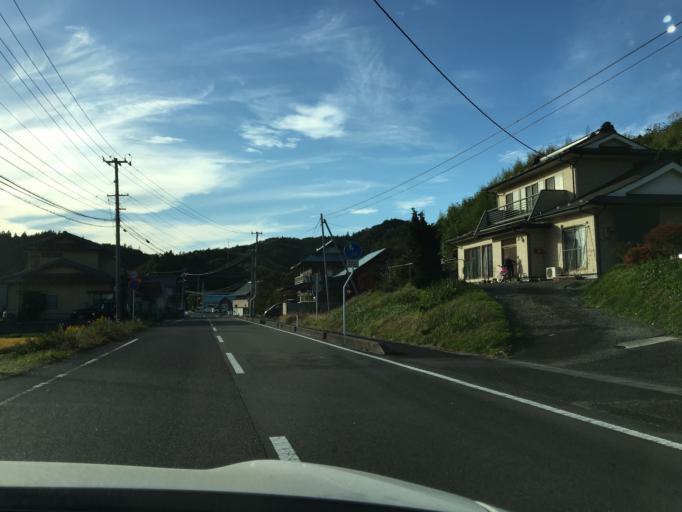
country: JP
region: Fukushima
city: Ishikawa
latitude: 37.2170
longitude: 140.5735
